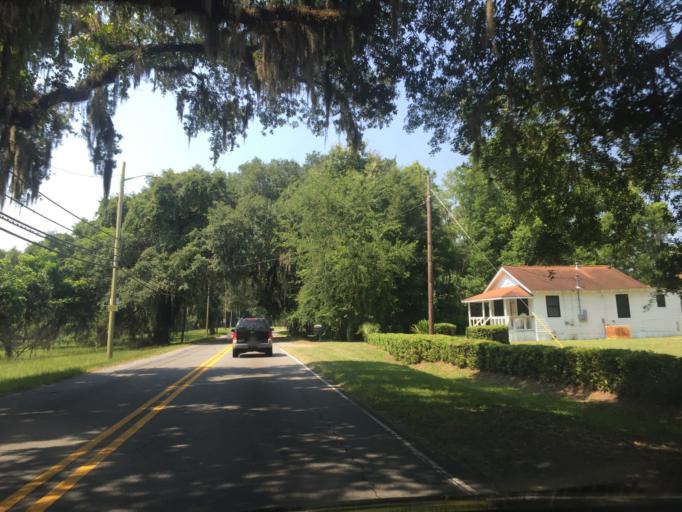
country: US
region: Georgia
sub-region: Chatham County
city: Montgomery
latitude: 31.9681
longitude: -81.1344
